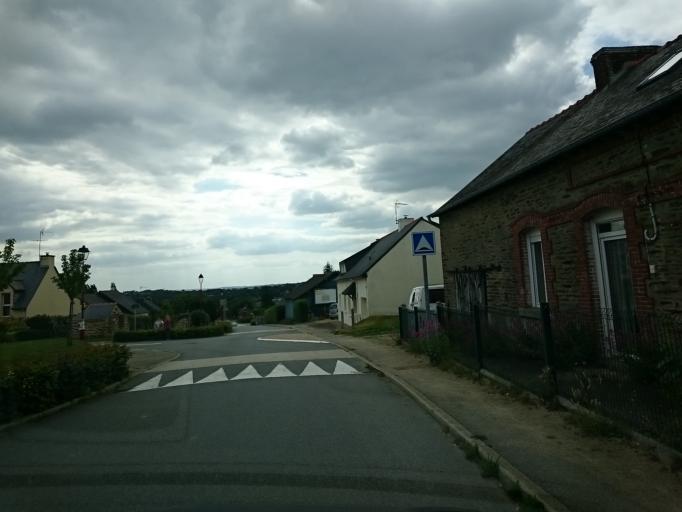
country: FR
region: Brittany
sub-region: Departement d'Ille-et-Vilaine
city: Chanteloup
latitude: 47.9278
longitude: -1.6095
